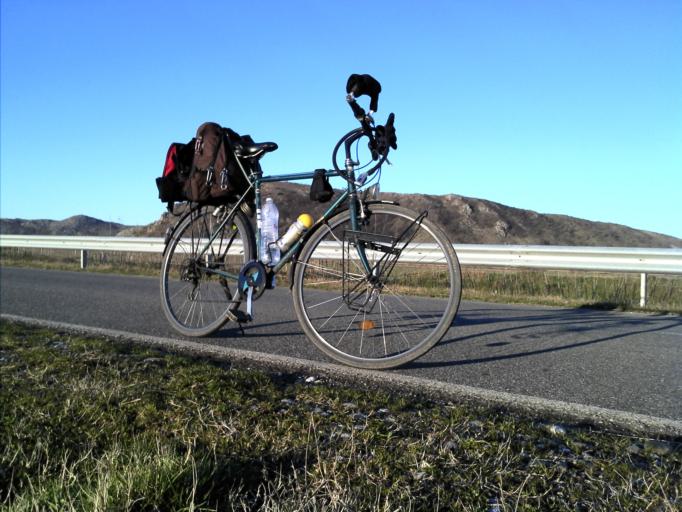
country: AL
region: Shkoder
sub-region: Rrethi i Shkodres
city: Dajc
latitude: 41.9377
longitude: 19.4439
